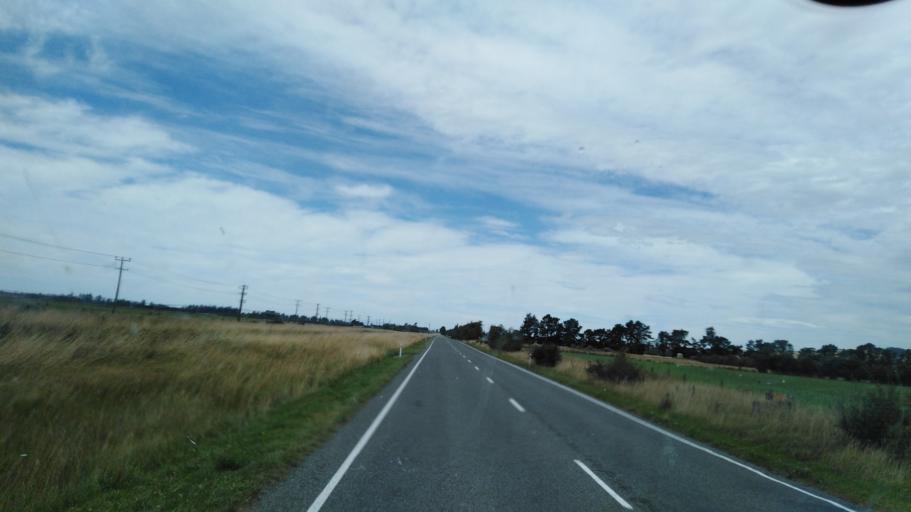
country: NZ
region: Canterbury
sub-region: Selwyn District
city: Darfield
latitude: -43.3634
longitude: 171.9745
